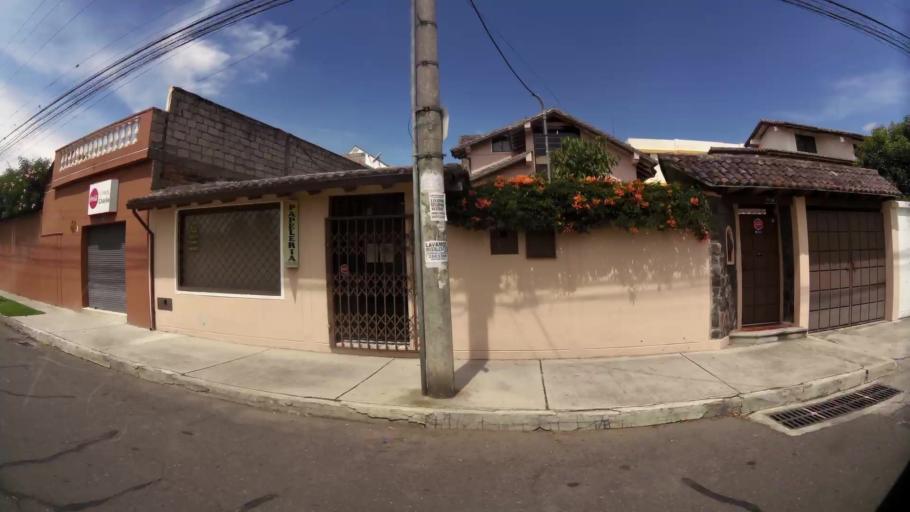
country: EC
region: Pichincha
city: Quito
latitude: -0.2124
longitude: -78.4272
